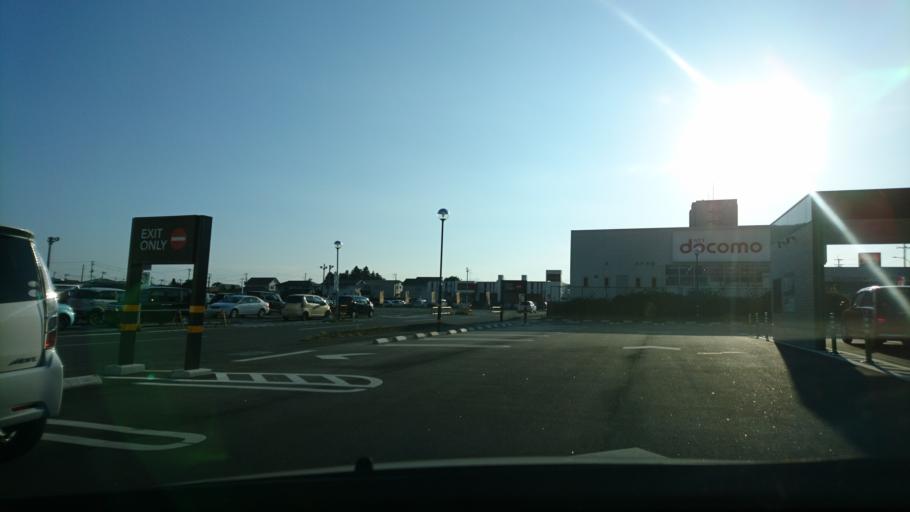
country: JP
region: Iwate
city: Ichinoseki
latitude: 38.9375
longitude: 141.1123
